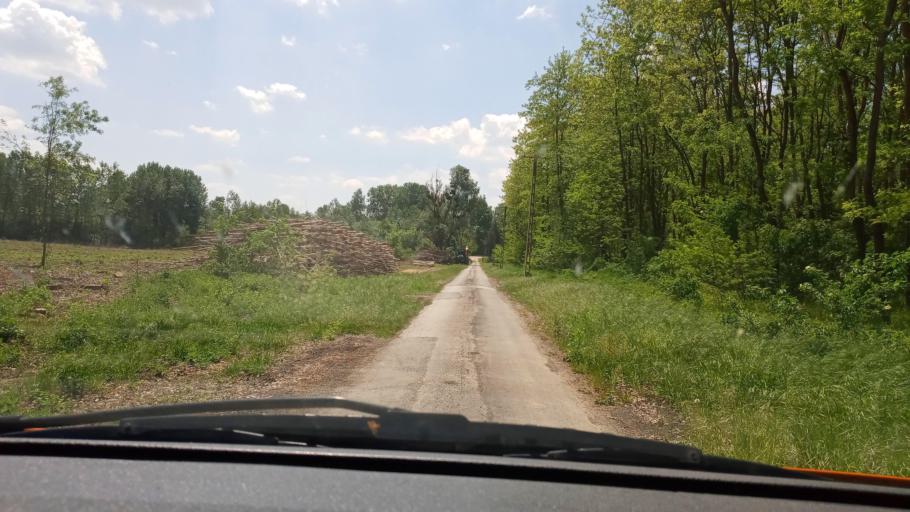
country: HU
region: Baranya
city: Siklos
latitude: 45.7679
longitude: 18.2871
